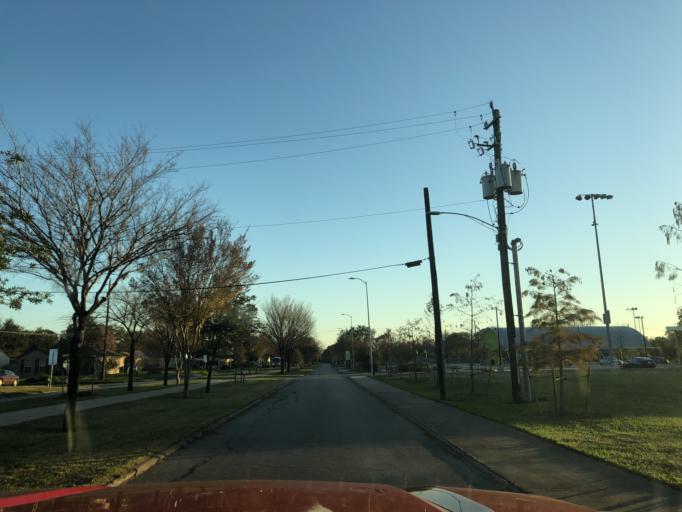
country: US
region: Texas
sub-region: Harris County
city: Jacinto City
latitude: 29.7647
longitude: -95.2701
